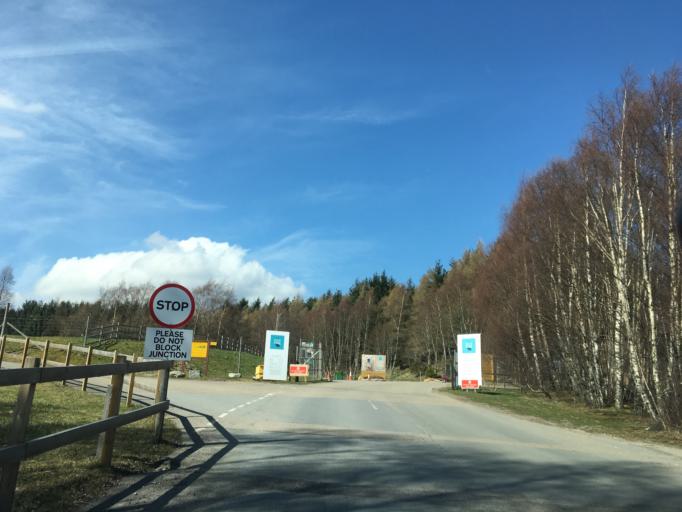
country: GB
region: Scotland
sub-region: Highland
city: Kingussie
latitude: 57.1096
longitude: -3.9673
